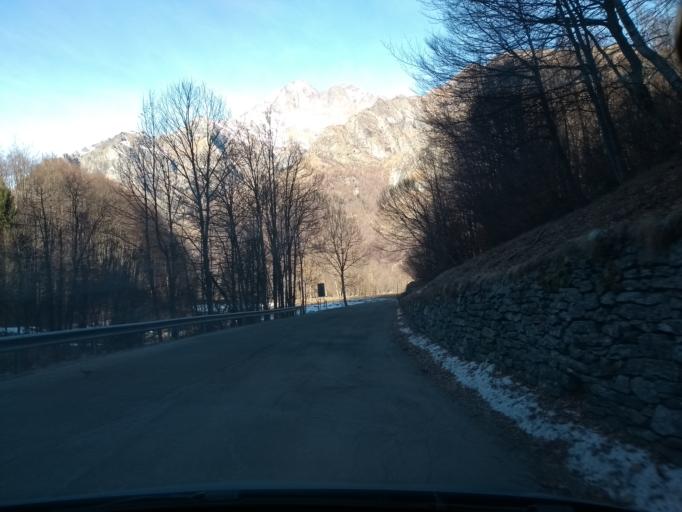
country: IT
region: Piedmont
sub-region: Provincia di Torino
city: Usseglio
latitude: 45.2233
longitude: 7.2485
